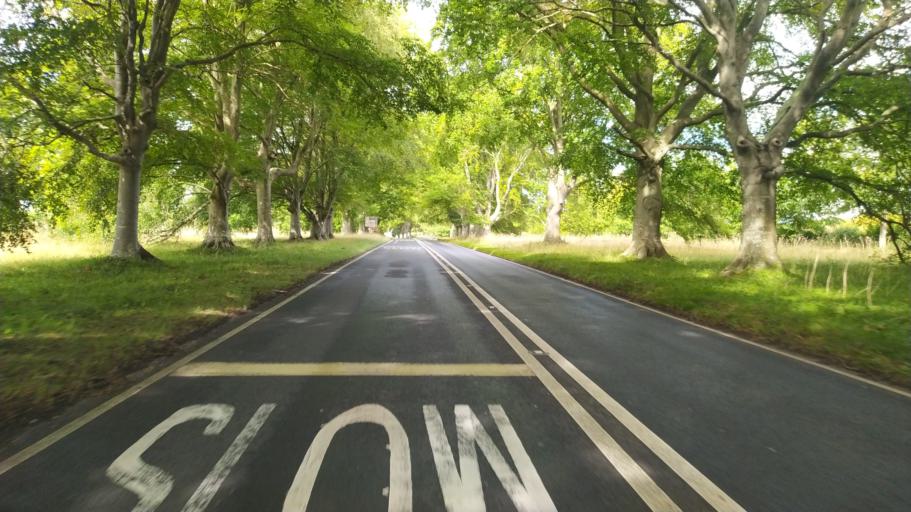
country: GB
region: England
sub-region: Dorset
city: Lytchett Matravers
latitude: 50.8195
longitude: -2.0468
